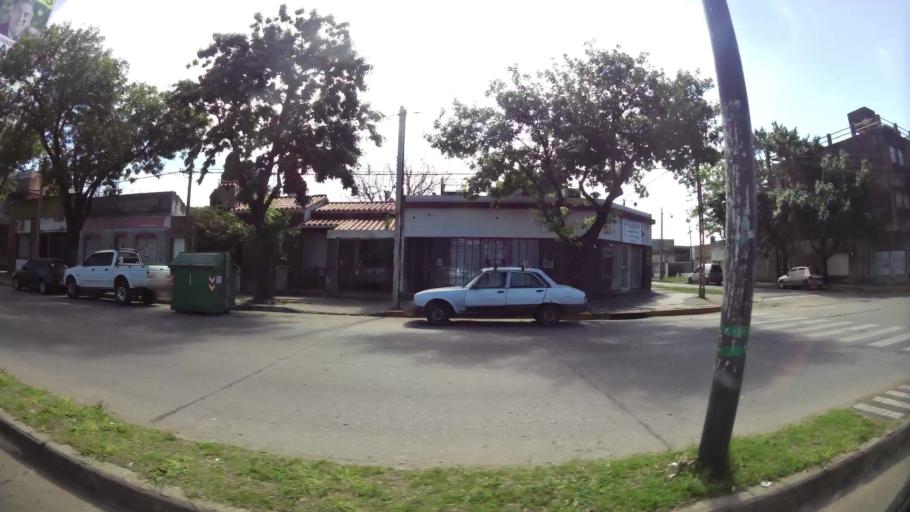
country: AR
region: Santa Fe
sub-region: Departamento de Rosario
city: Rosario
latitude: -32.9358
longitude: -60.7129
